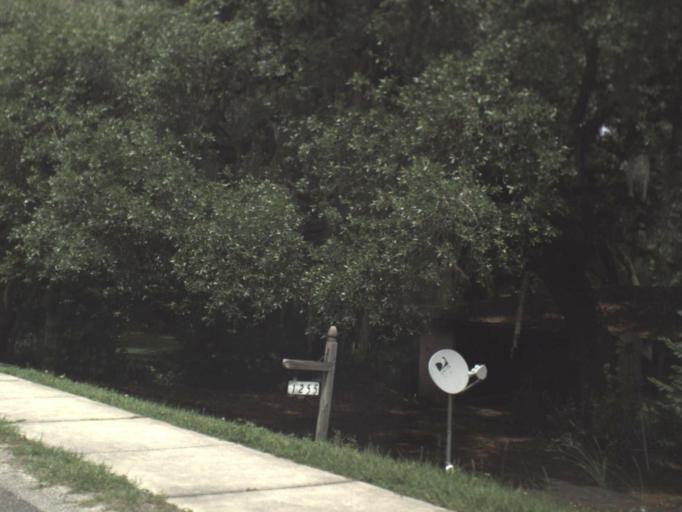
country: US
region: Florida
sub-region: Clay County
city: Keystone Heights
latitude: 29.7720
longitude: -82.0358
